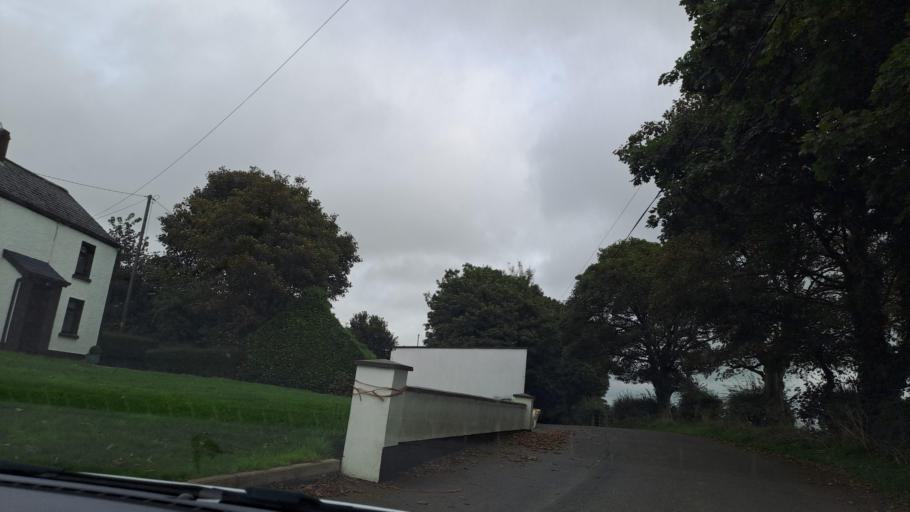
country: IE
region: Ulster
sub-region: County Monaghan
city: Carrickmacross
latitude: 54.0335
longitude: -6.7740
